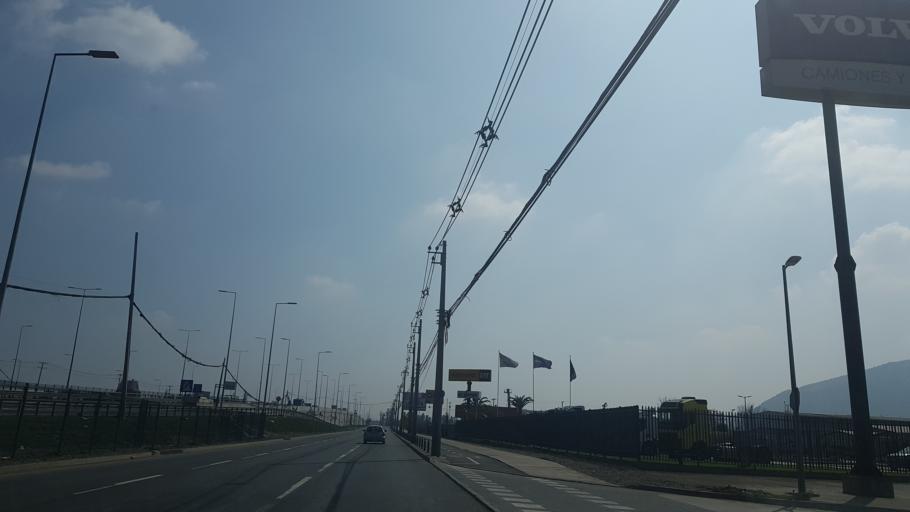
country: CL
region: Santiago Metropolitan
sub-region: Provincia de Chacabuco
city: Chicureo Abajo
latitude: -33.3515
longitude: -70.7064
